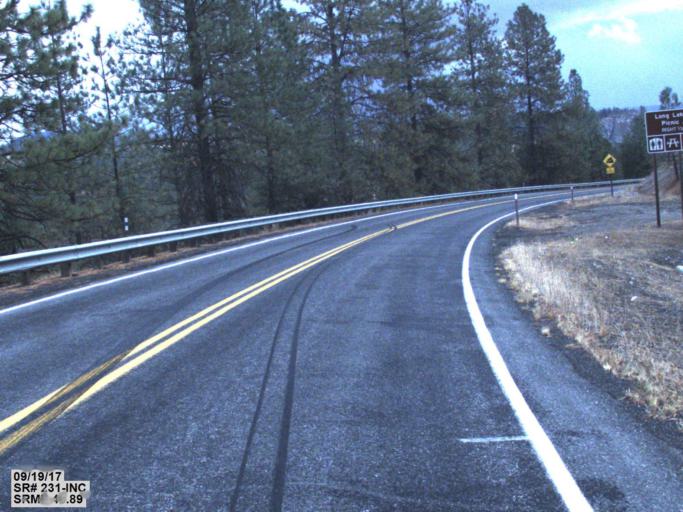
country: US
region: Washington
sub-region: Spokane County
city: Fairchild Air Force Base
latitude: 47.8400
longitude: -117.8665
